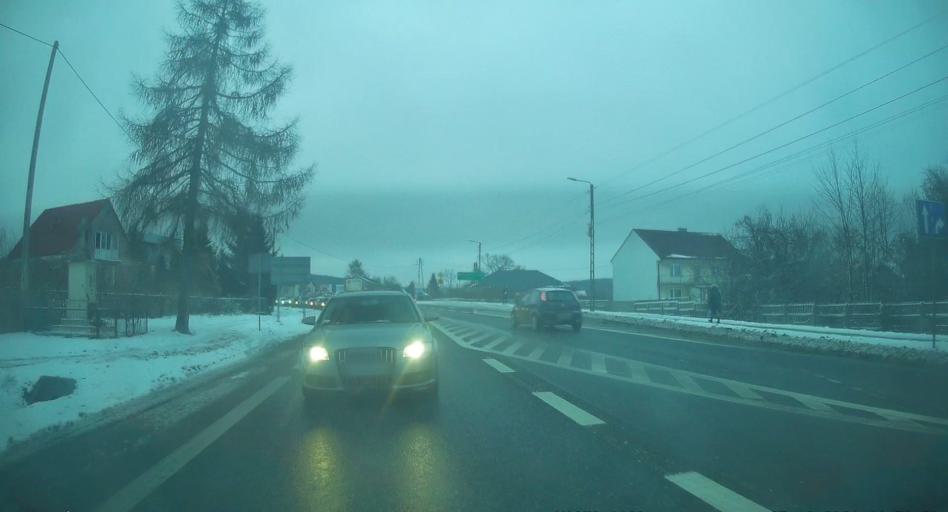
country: PL
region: Swietokrzyskie
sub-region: Powiat kielecki
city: Kostomloty Drugie
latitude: 50.9300
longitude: 20.5654
